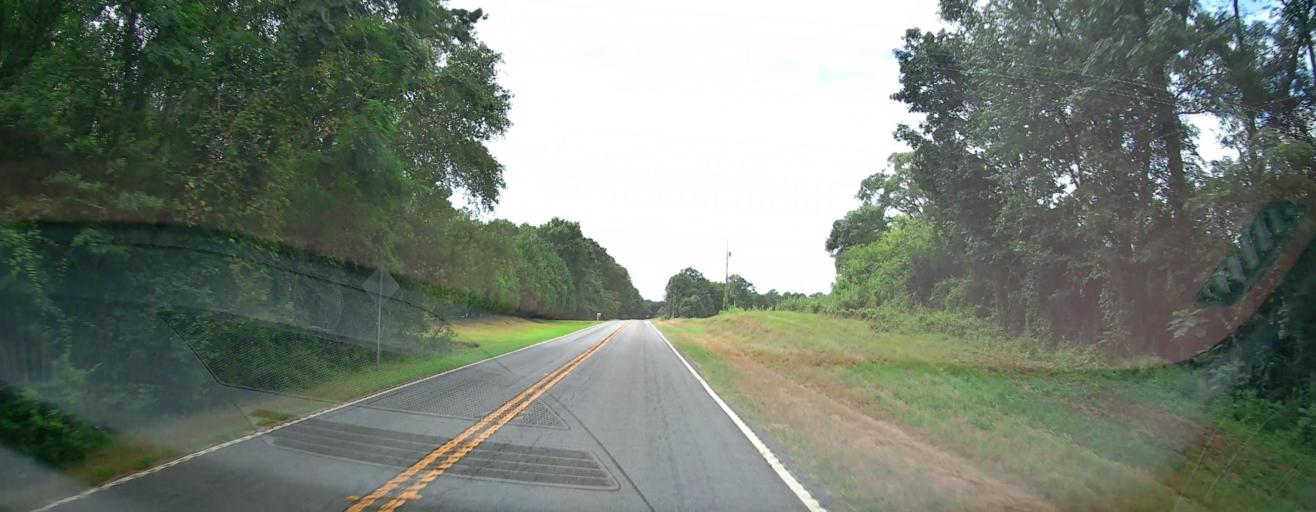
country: US
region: Georgia
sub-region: Macon County
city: Montezuma
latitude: 32.2941
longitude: -83.9073
